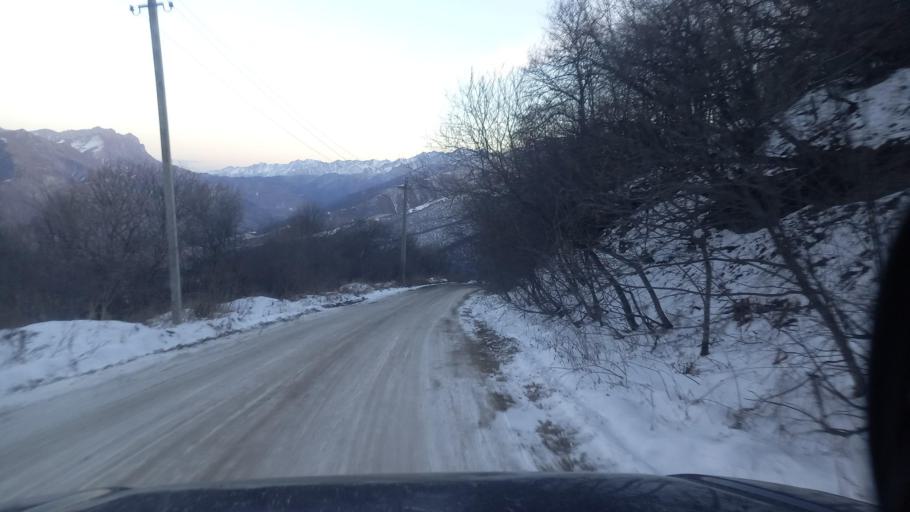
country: RU
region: Ingushetiya
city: Dzhayrakh
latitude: 42.8328
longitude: 44.5690
